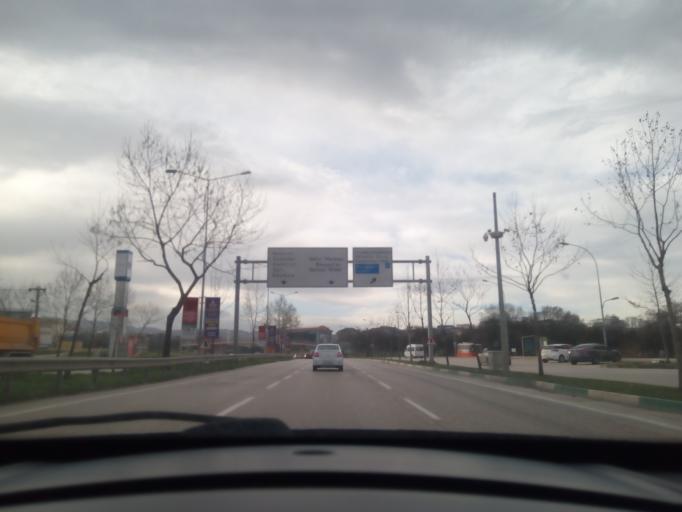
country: TR
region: Bursa
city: Cali
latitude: 40.2162
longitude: 28.9521
